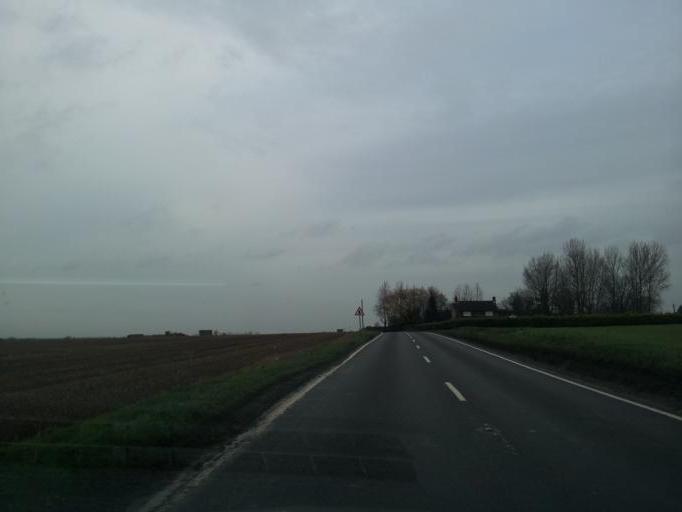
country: GB
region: England
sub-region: Norfolk
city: Martham
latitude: 52.6843
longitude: 1.5952
